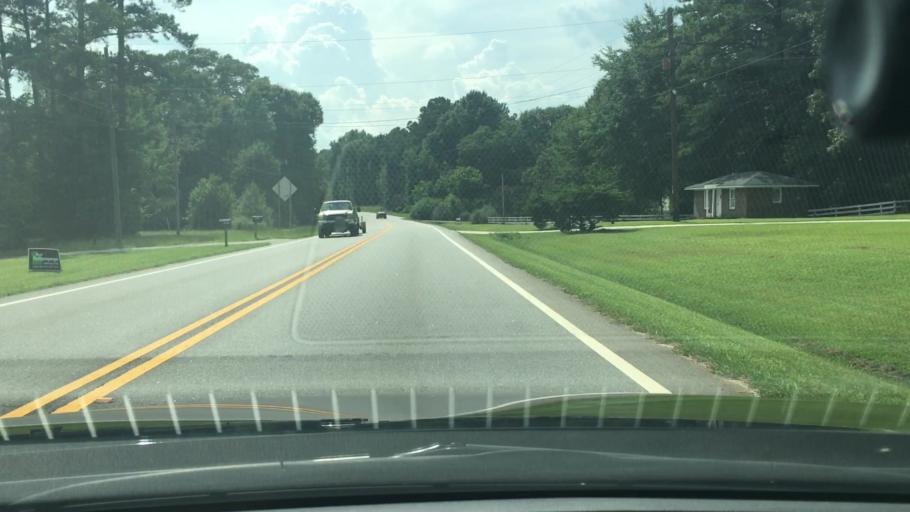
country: US
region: Georgia
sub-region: Coweta County
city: East Newnan
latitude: 33.3353
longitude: -84.7209
